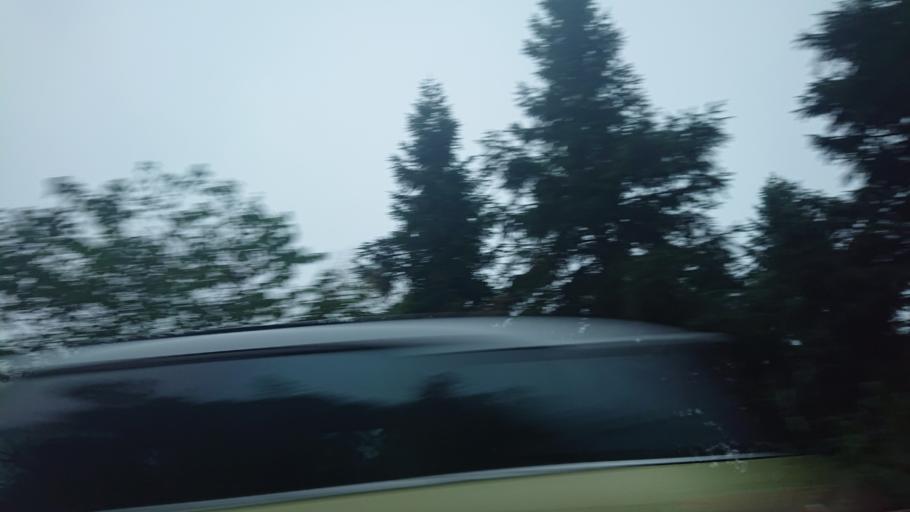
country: TW
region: Taiwan
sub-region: Chiayi
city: Jiayi Shi
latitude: 23.4803
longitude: 120.6960
